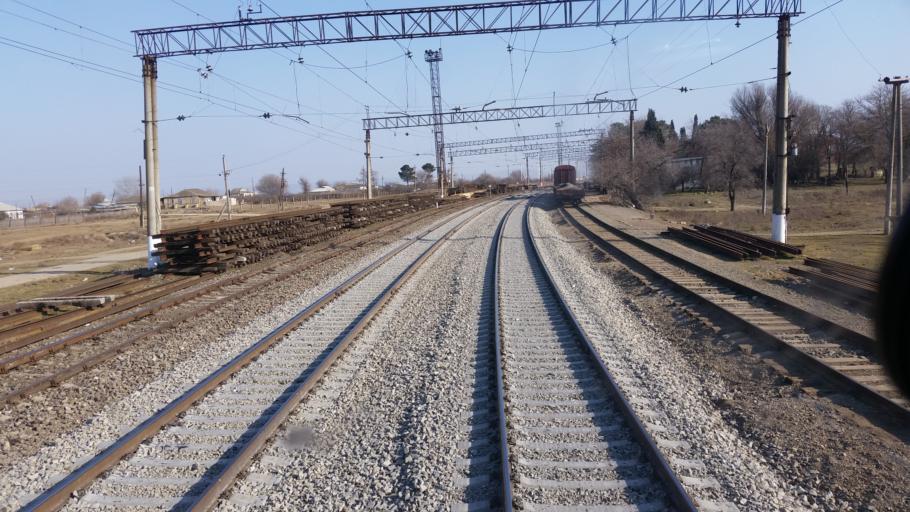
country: AZ
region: Haciqabul
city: Haciqabul
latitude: 40.0500
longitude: 49.0454
